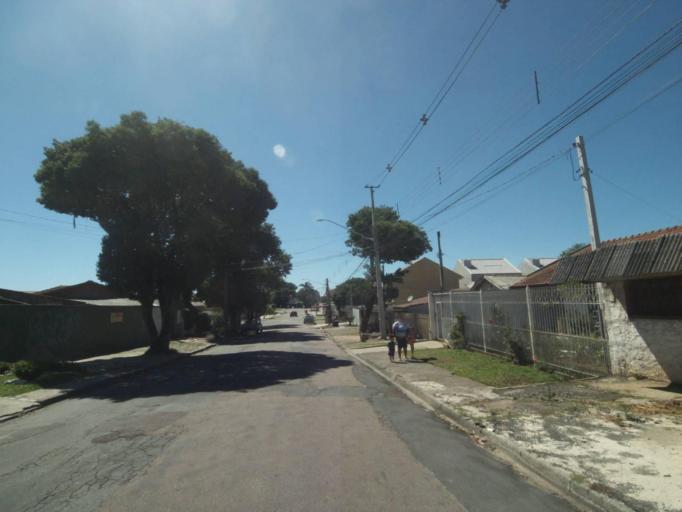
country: BR
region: Parana
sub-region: Curitiba
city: Curitiba
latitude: -25.4787
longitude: -49.3388
